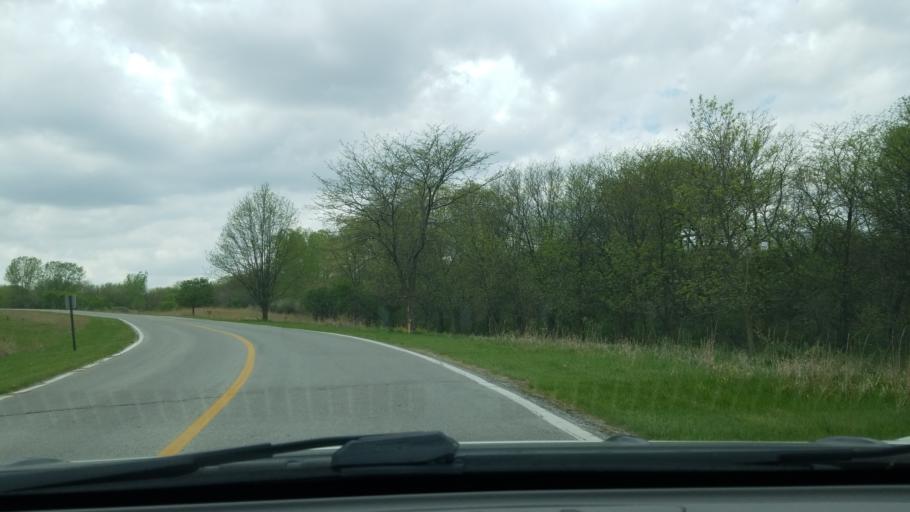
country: US
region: Nebraska
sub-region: Sarpy County
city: Chalco
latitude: 41.1709
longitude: -96.1637
